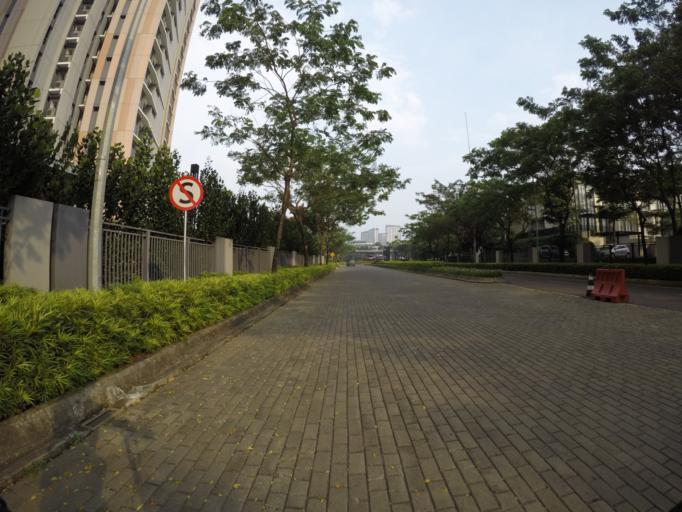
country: ID
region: West Java
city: Serpong
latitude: -6.2976
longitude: 106.6505
